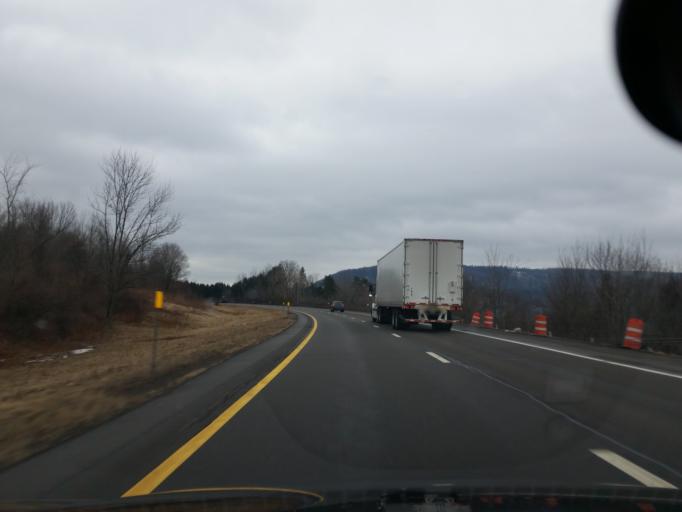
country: US
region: Pennsylvania
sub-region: Susquehanna County
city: Hallstead
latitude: 42.0221
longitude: -75.7849
